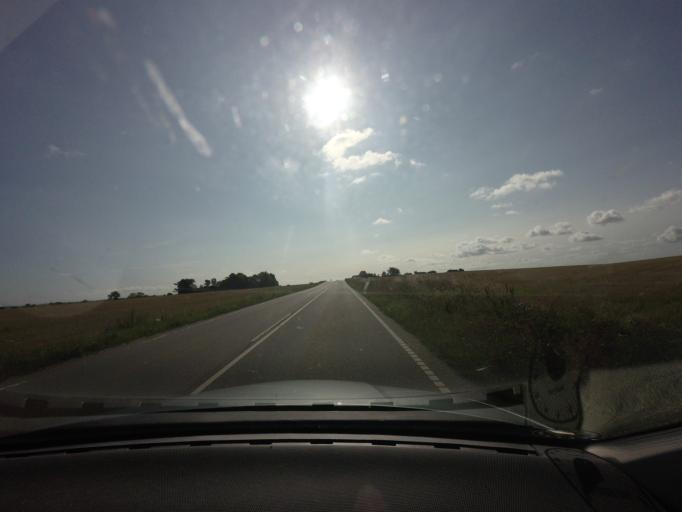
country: DK
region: Zealand
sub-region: Vordingborg Kommune
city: Stege
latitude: 55.0038
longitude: 12.1509
